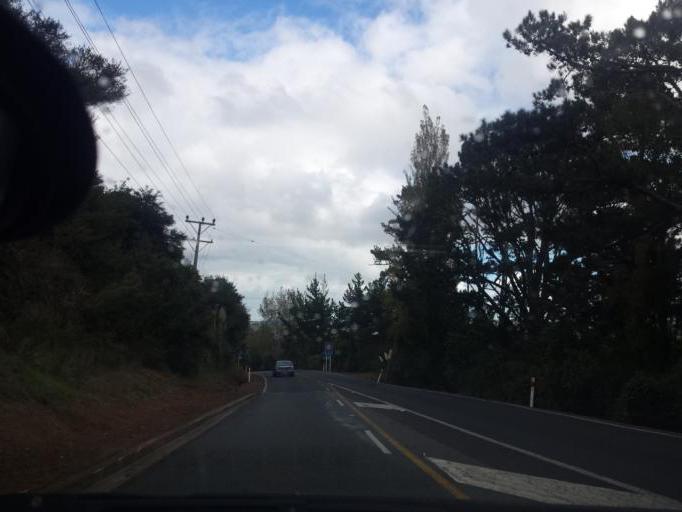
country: NZ
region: Auckland
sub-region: Auckland
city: Warkworth
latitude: -36.4082
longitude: 174.7194
